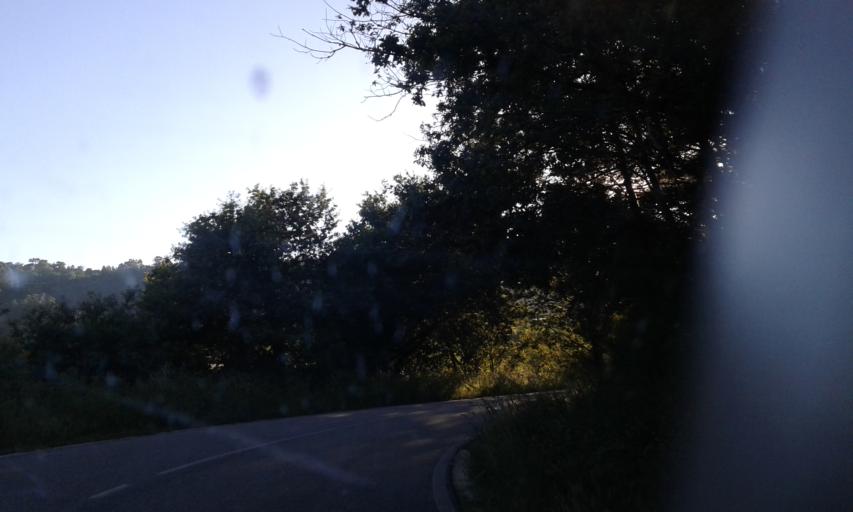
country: ES
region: Galicia
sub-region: Provincia de Pontevedra
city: Oia
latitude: 41.9943
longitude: -8.8163
